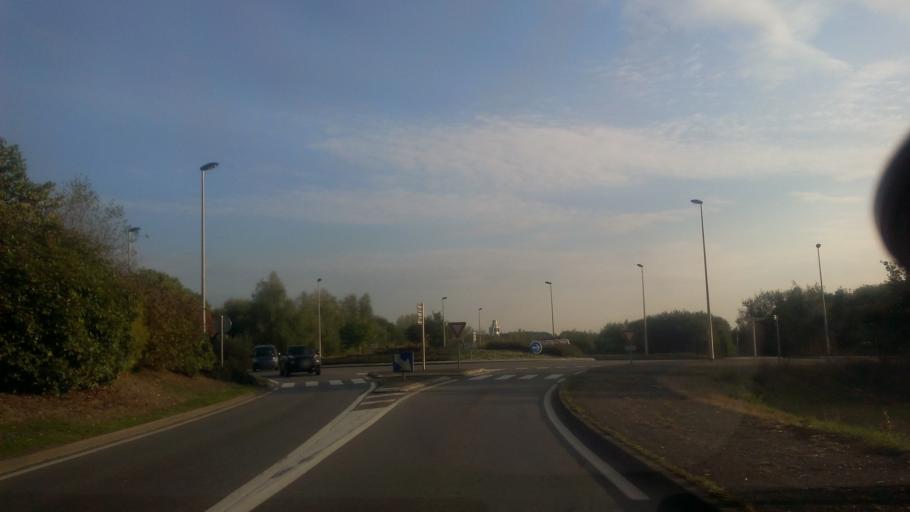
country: FR
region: Brittany
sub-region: Departement d'Ille-et-Vilaine
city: Redon
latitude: 47.6489
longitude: -2.0982
